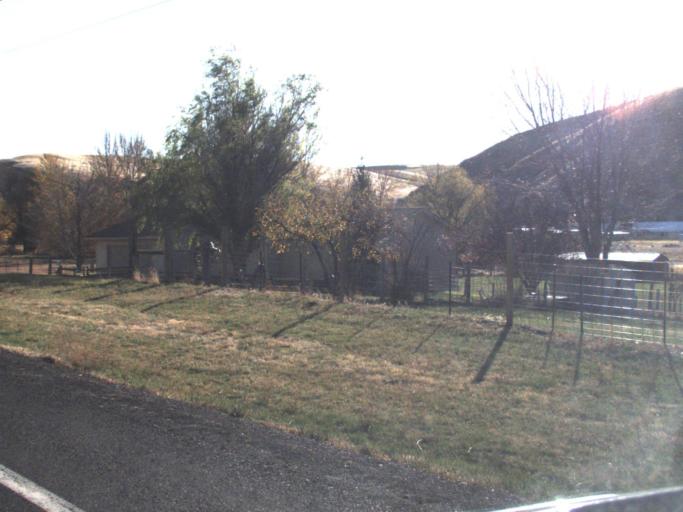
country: US
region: Washington
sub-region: Garfield County
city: Pomeroy
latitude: 46.4746
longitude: -117.5512
